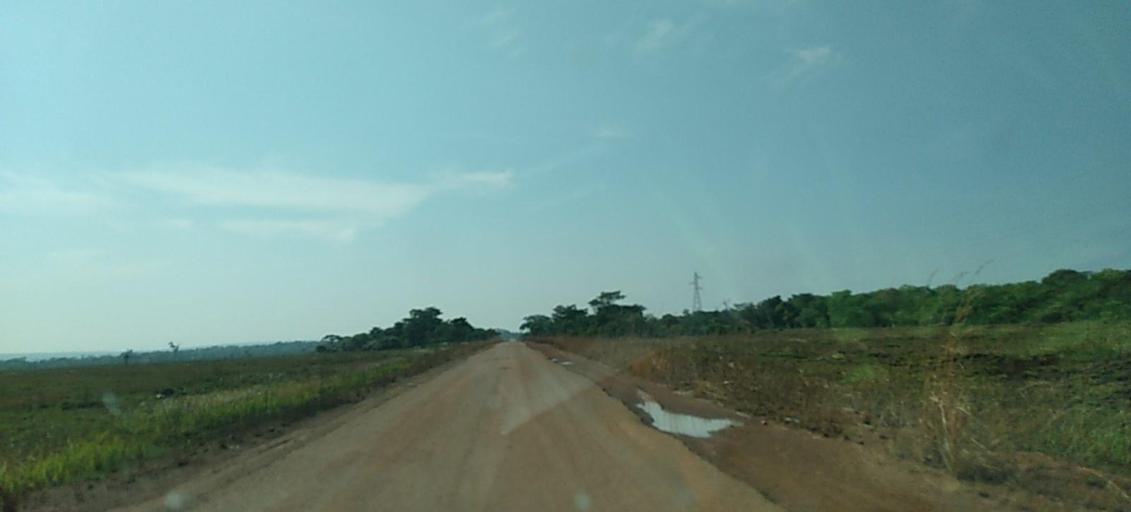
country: ZM
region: North-Western
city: Mwinilunga
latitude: -11.8119
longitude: 25.0862
